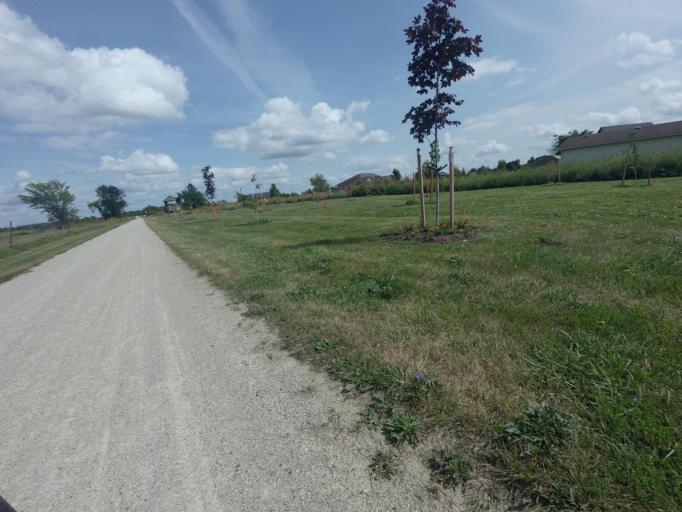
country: CA
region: Ontario
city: Waterloo
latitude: 43.5840
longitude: -80.7230
